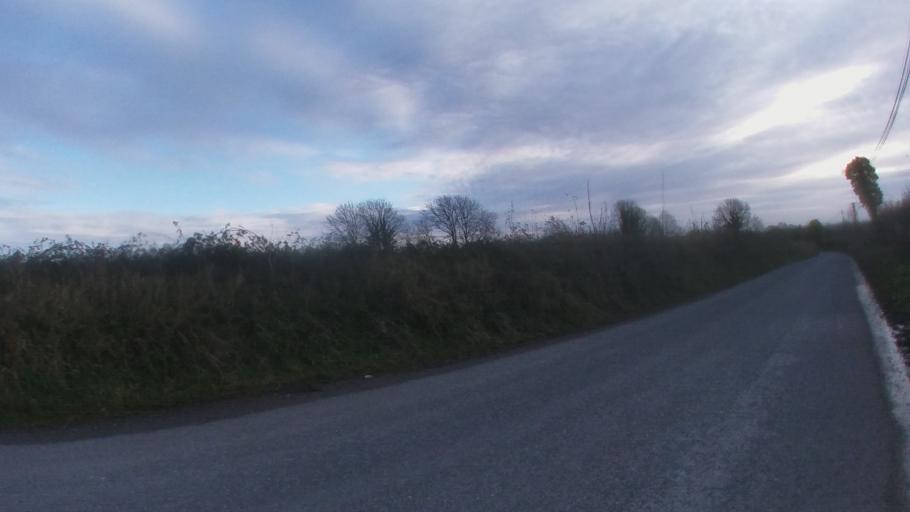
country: IE
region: Leinster
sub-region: Kilkenny
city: Kilkenny
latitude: 52.6890
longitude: -7.1753
